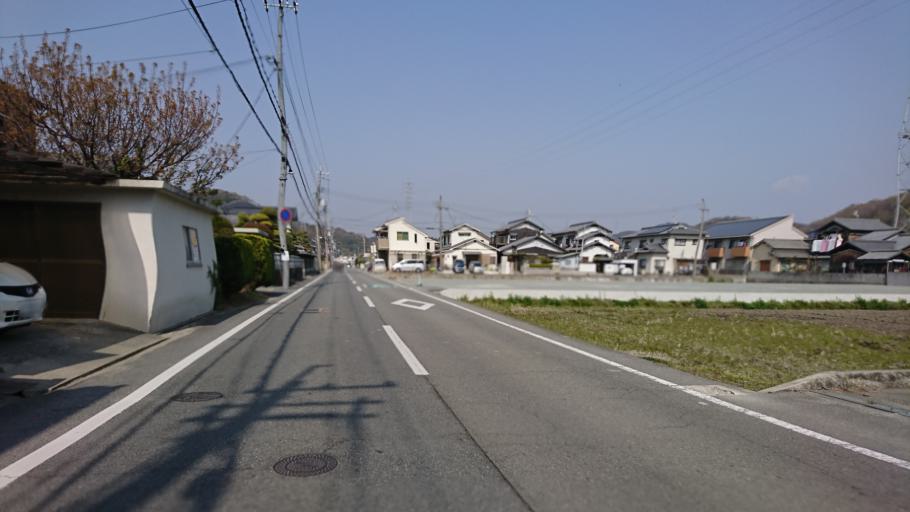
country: JP
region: Hyogo
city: Shirahamacho-usazakiminami
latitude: 34.7875
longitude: 134.7549
